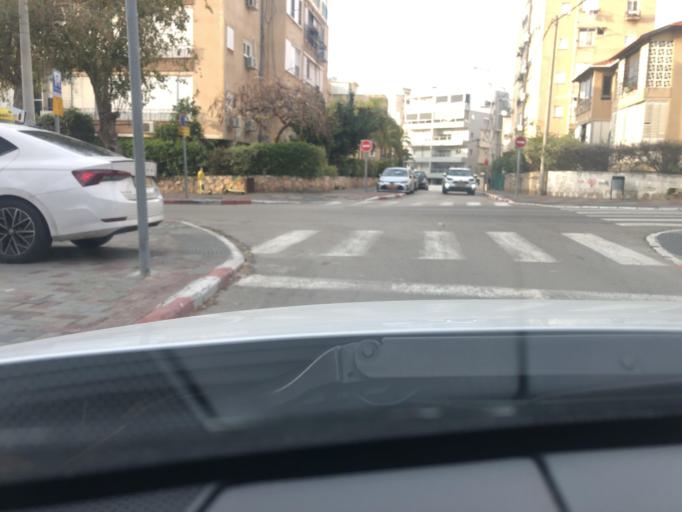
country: IL
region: Tel Aviv
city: Bat Yam
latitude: 32.0209
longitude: 34.7480
